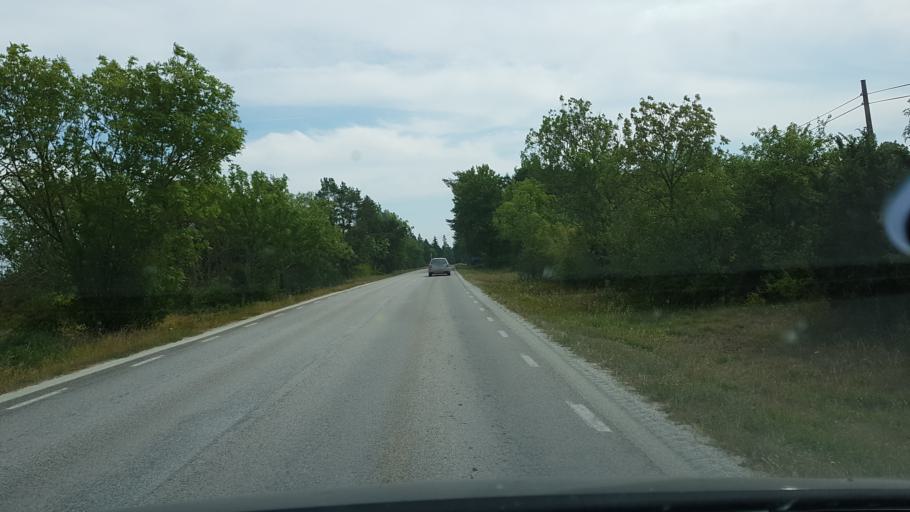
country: SE
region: Gotland
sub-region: Gotland
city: Slite
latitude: 57.7465
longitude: 18.7348
